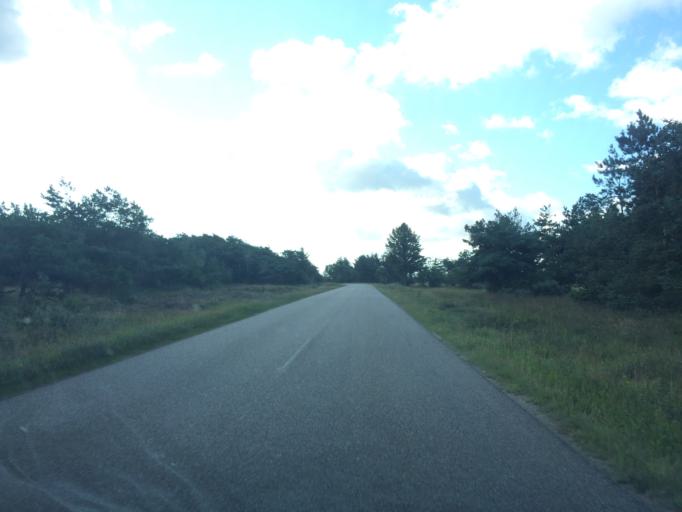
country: DK
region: South Denmark
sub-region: Varde Kommune
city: Oksbol
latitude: 55.6706
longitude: 8.1912
